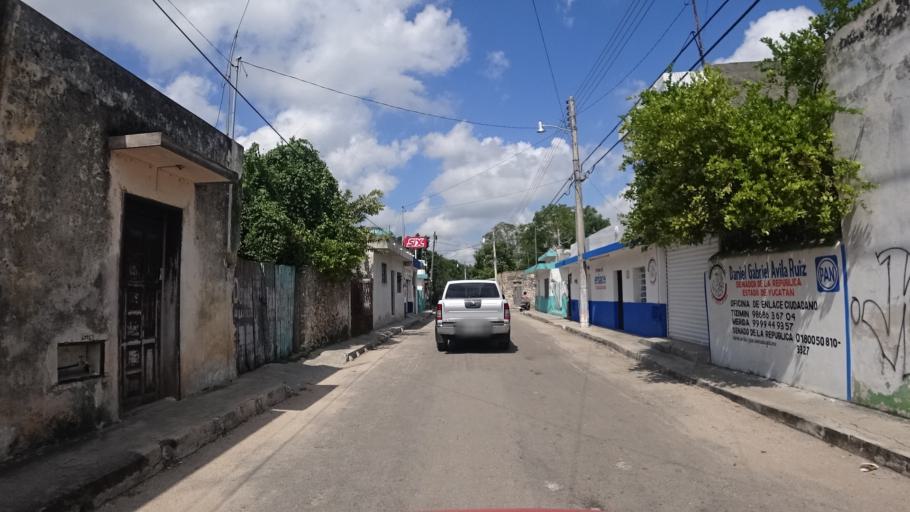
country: MX
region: Yucatan
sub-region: Tizimin
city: Tizimin
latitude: 21.1461
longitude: -88.1524
